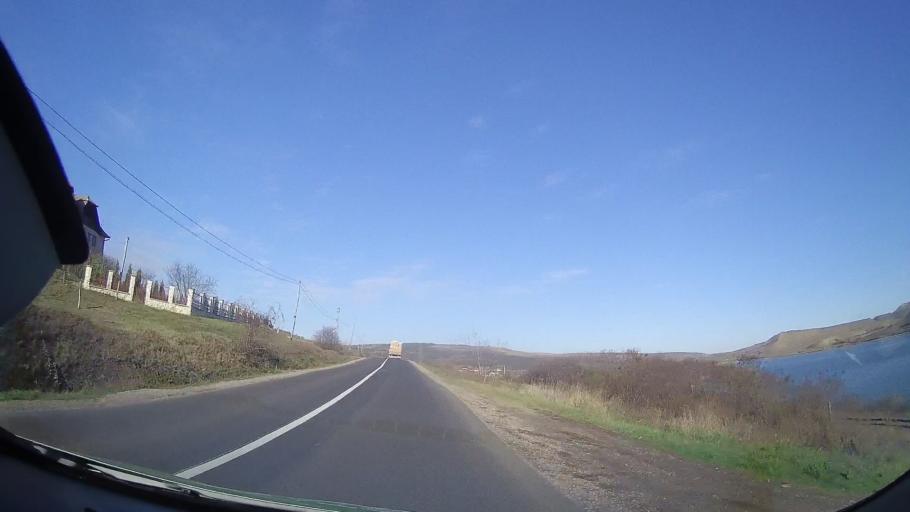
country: RO
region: Mures
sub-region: Comuna Zau De Campie
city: Zau de Campie
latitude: 46.6265
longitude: 24.1330
